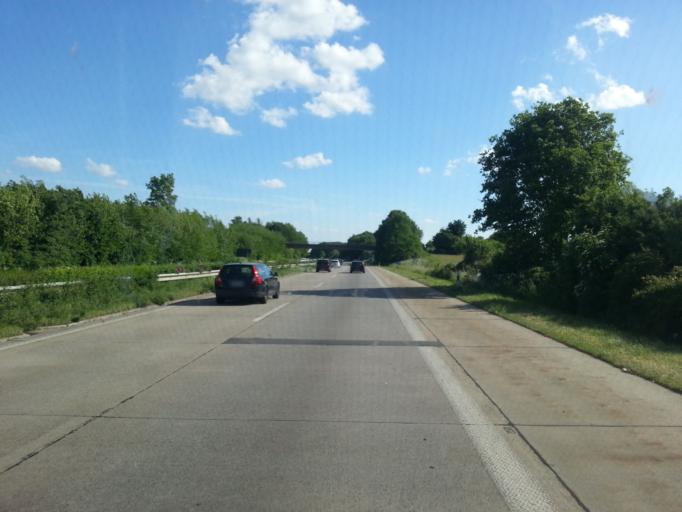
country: DE
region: Schleswig-Holstein
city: Scharbeutz
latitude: 54.0138
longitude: 10.7290
